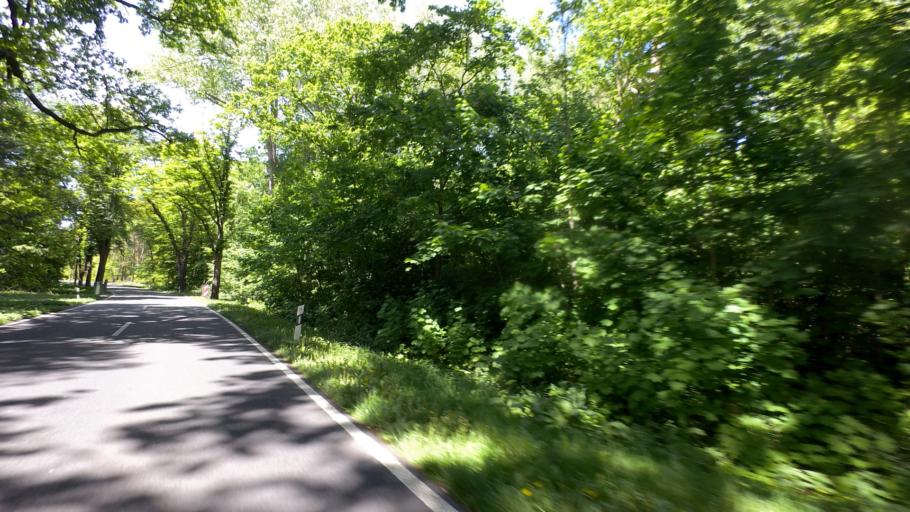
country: DE
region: Brandenburg
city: Baruth
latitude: 52.0839
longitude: 13.4443
